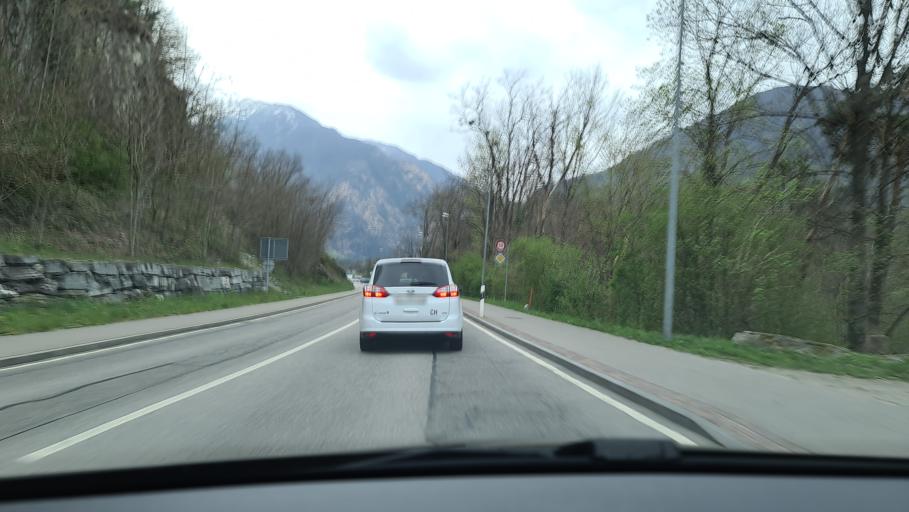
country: CH
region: Ticino
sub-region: Locarno District
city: Verscio
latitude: 46.2391
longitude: 8.7145
